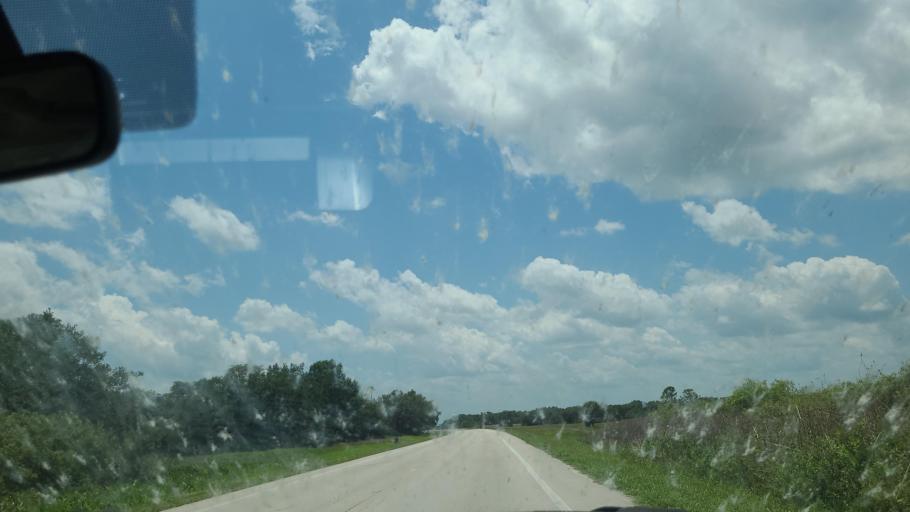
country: US
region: Florida
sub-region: Glades County
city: Buckhead Ridge
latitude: 27.1022
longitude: -81.0698
